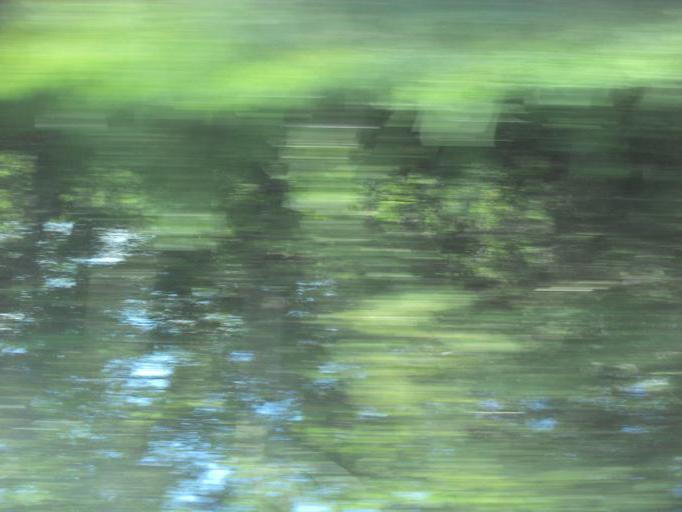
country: MX
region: Chiapas
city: Palenque
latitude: 17.5525
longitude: -91.9955
